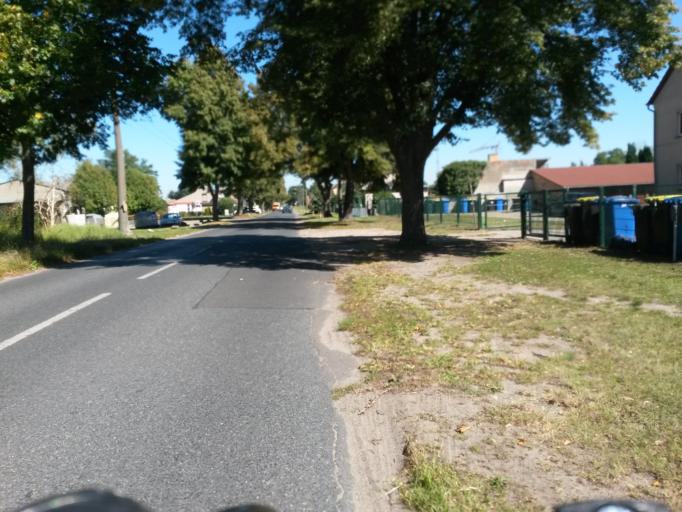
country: DE
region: Brandenburg
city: Oderberg
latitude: 52.8446
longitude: 14.1190
